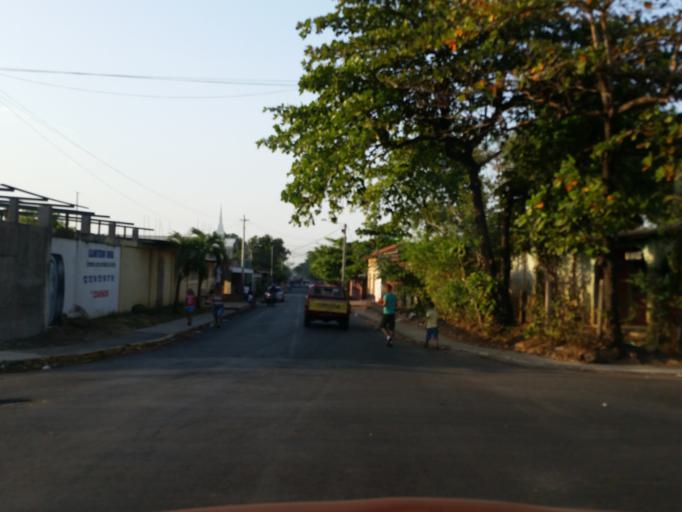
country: NI
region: Managua
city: Managua
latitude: 12.1400
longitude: -86.2541
